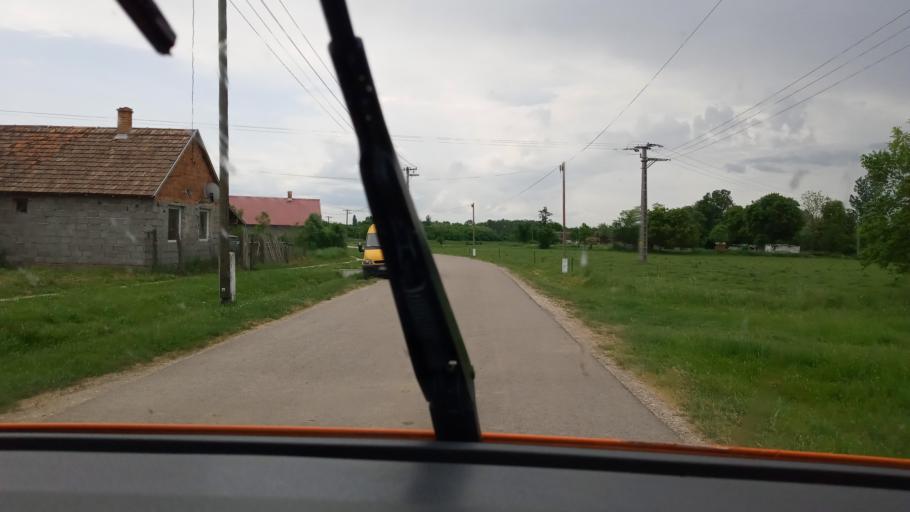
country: HU
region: Baranya
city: Vajszlo
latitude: 45.8236
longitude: 17.9935
